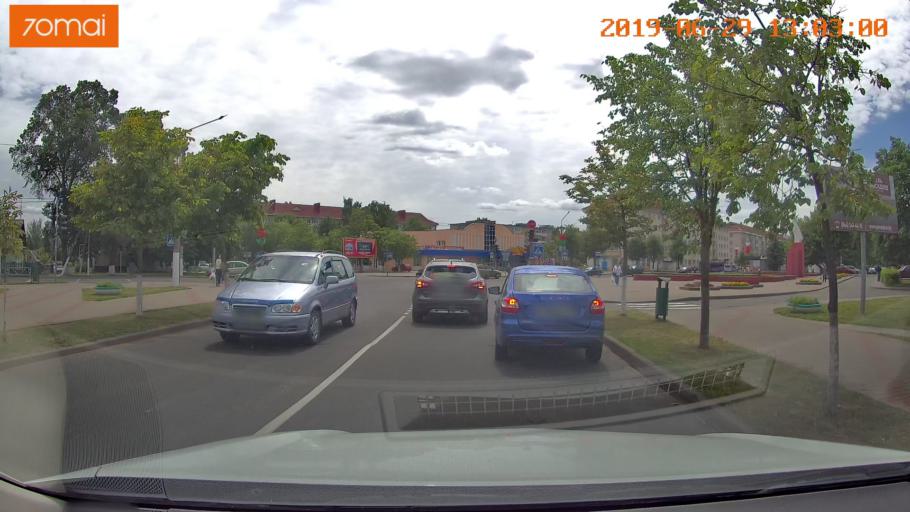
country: BY
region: Minsk
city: Slutsk
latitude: 53.0332
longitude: 27.5601
